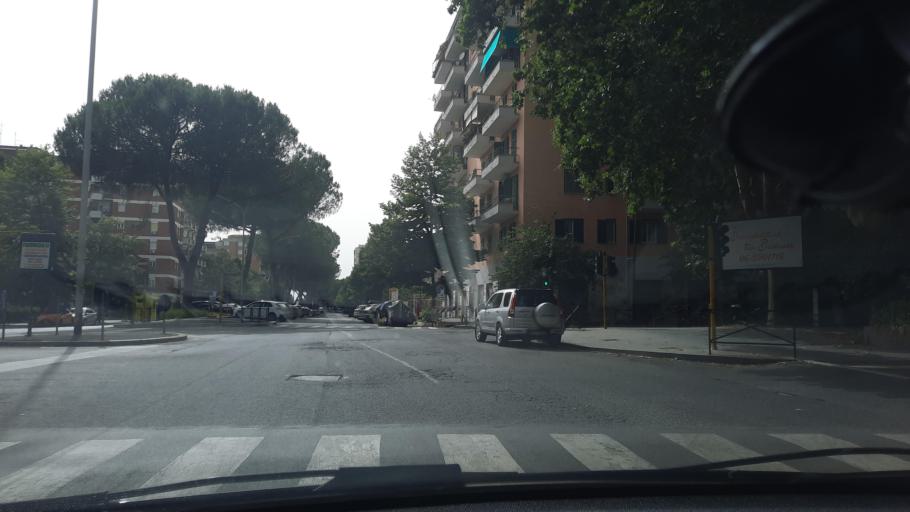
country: IT
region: Latium
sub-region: Citta metropolitana di Roma Capitale
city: Rome
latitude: 41.8560
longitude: 12.4847
